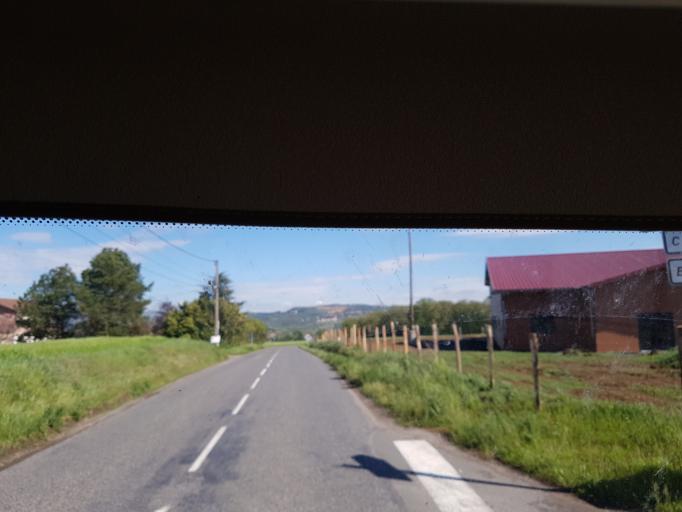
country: FR
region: Rhone-Alpes
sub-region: Departement du Rhone
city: Lentilly
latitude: 45.8337
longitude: 4.6697
